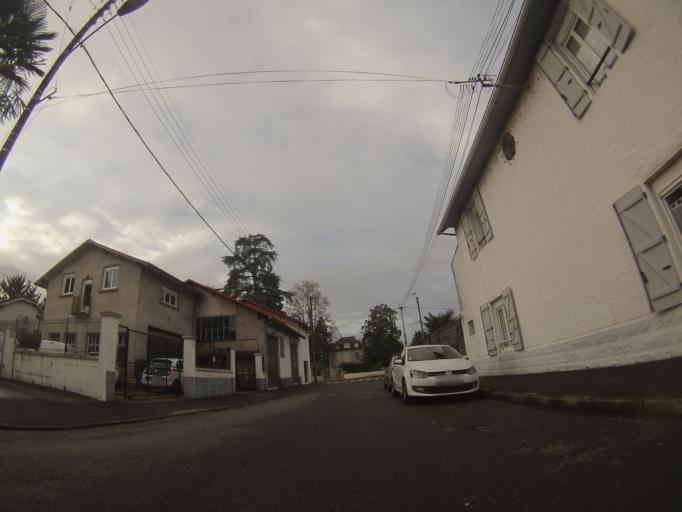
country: FR
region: Aquitaine
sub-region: Departement des Pyrenees-Atlantiques
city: Jurancon
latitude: 43.2846
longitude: -0.3838
